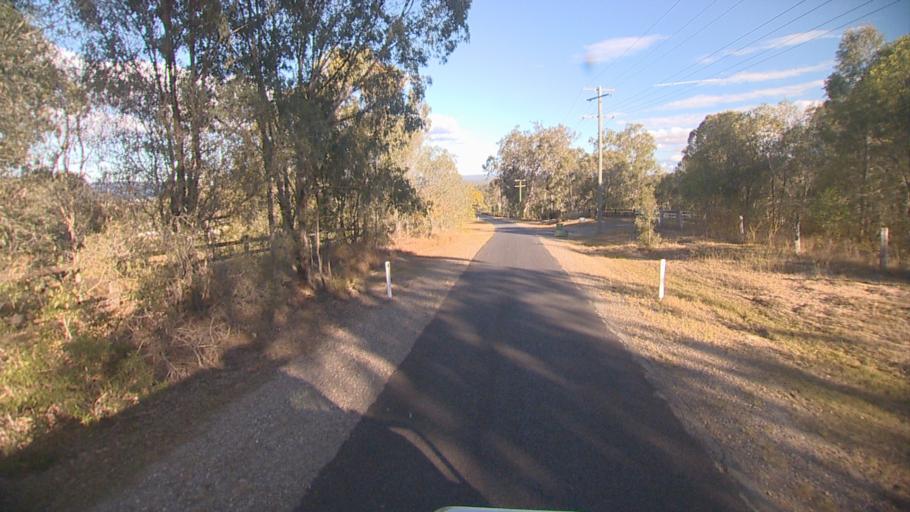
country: AU
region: Queensland
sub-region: Logan
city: Cedar Vale
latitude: -27.9248
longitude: 153.0666
